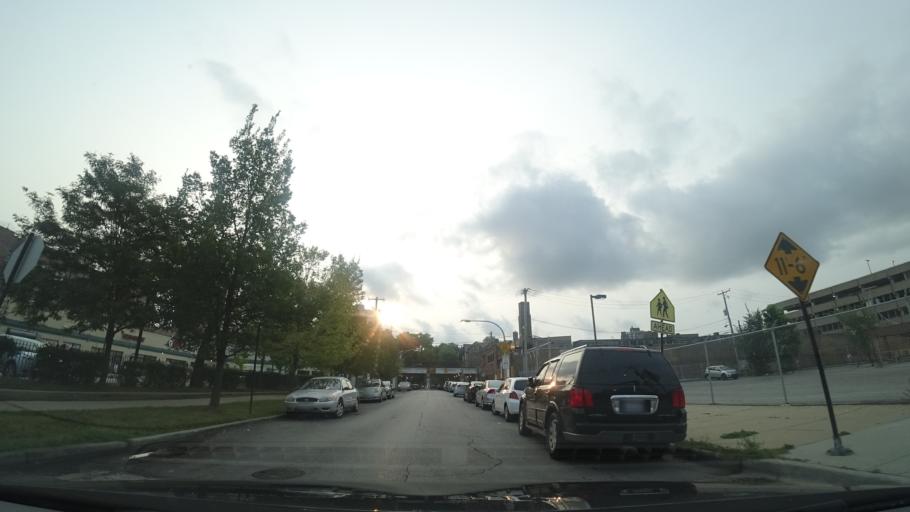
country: US
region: Illinois
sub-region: Cook County
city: Evanston
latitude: 41.9752
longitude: -87.6597
